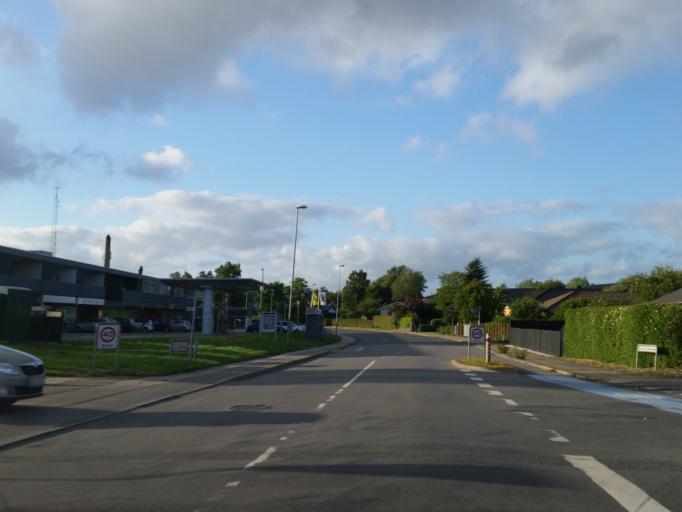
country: DK
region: South Denmark
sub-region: Vejle Kommune
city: Brejning
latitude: 55.6609
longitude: 9.6736
